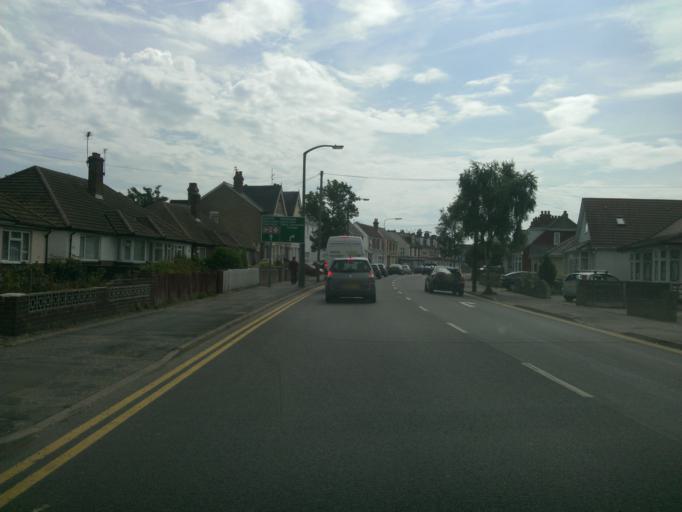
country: GB
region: England
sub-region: Essex
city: Clacton-on-Sea
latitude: 51.7988
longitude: 1.1525
